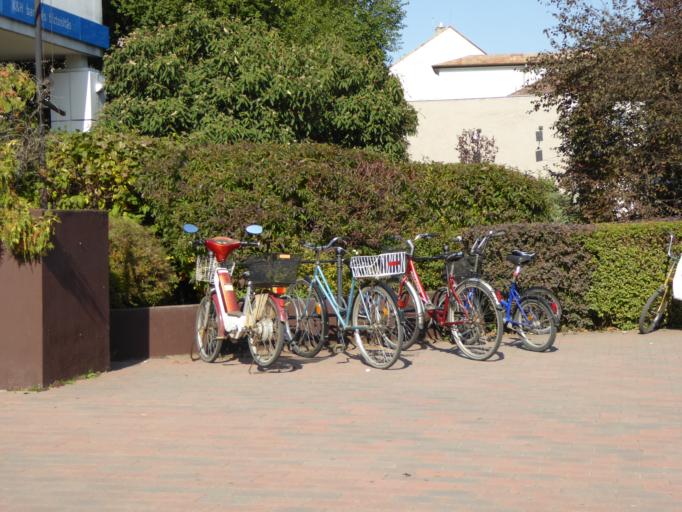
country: HU
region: Hajdu-Bihar
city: Berettyoujfalu
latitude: 47.2205
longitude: 21.5363
